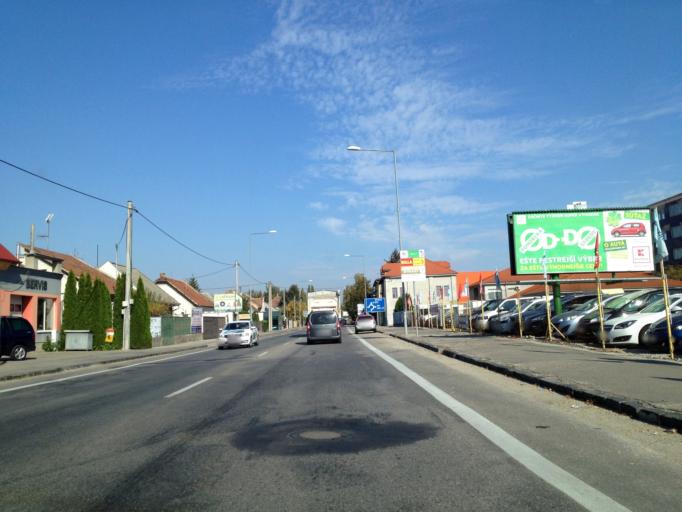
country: SK
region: Nitriansky
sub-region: Okres Nove Zamky
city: Nove Zamky
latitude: 47.9810
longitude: 18.1767
